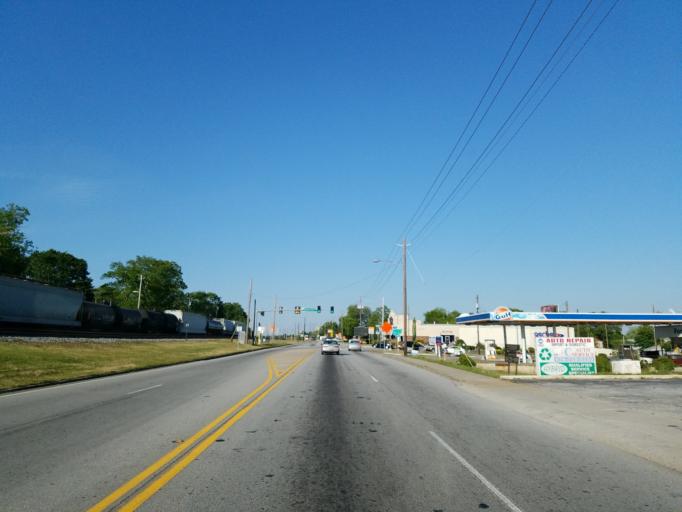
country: US
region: Georgia
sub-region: Douglas County
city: Douglasville
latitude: 33.7536
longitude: -84.7428
